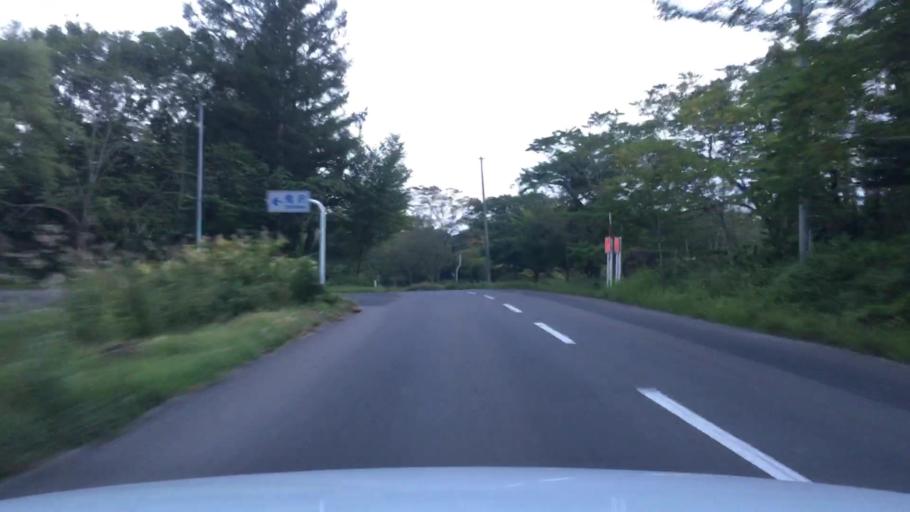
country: JP
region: Aomori
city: Shimokizukuri
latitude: 40.6885
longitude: 140.3628
